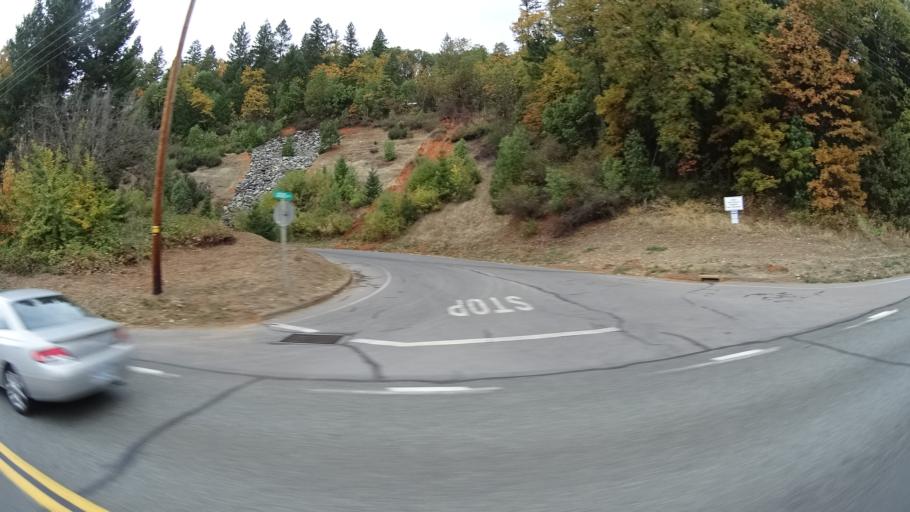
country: US
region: California
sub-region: Siskiyou County
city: Happy Camp
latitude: 41.8025
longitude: -123.3728
